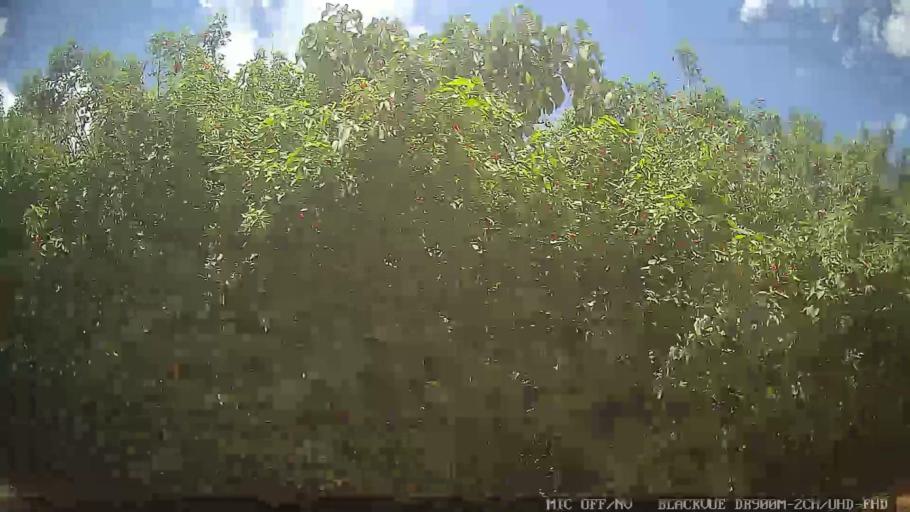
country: BR
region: Sao Paulo
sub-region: Braganca Paulista
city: Braganca Paulista
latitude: -23.0115
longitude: -46.4741
